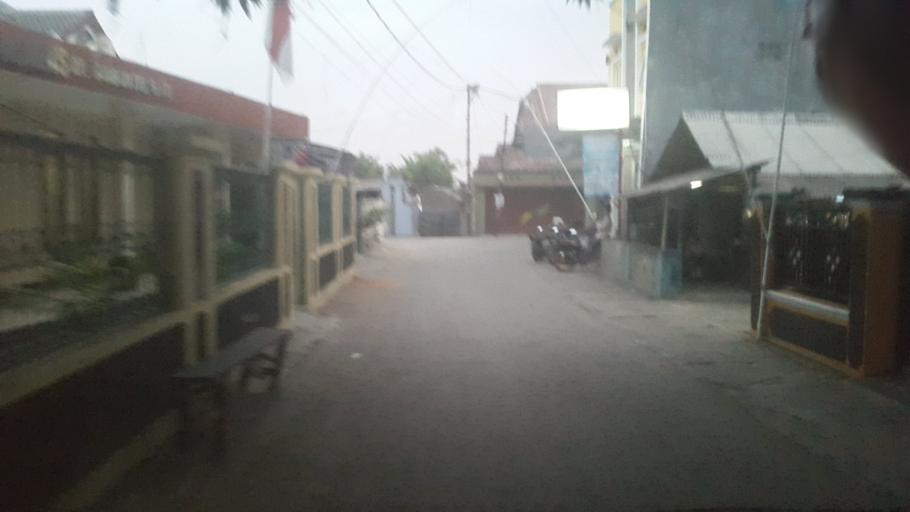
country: ID
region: West Java
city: Pelabuhanratu
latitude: -6.9902
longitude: 106.5495
